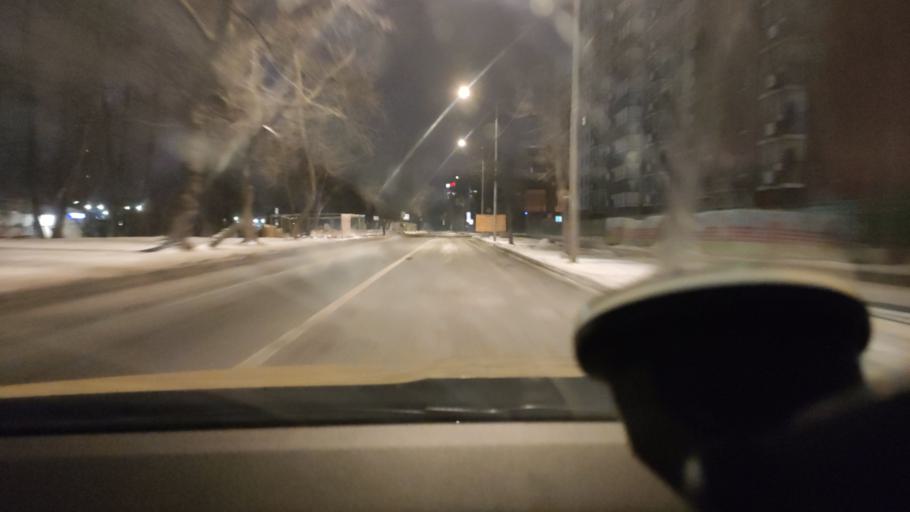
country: RU
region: Moscow
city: Ryazanskiy
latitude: 55.7393
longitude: 37.7359
